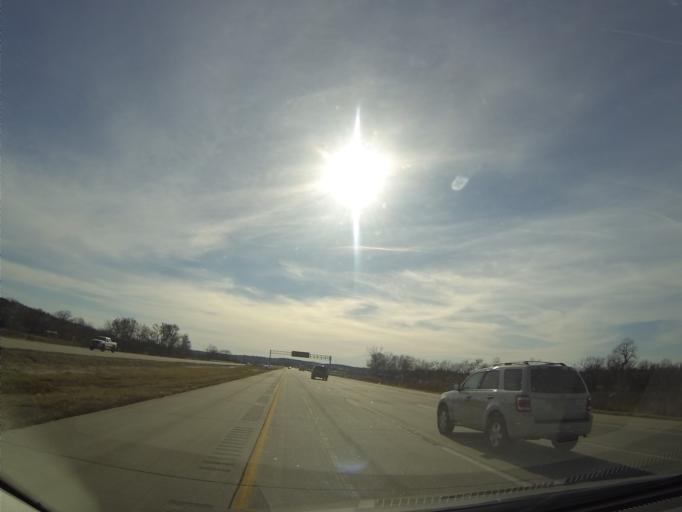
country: US
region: Nebraska
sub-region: Saunders County
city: Ashland
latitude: 41.0426
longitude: -96.2939
